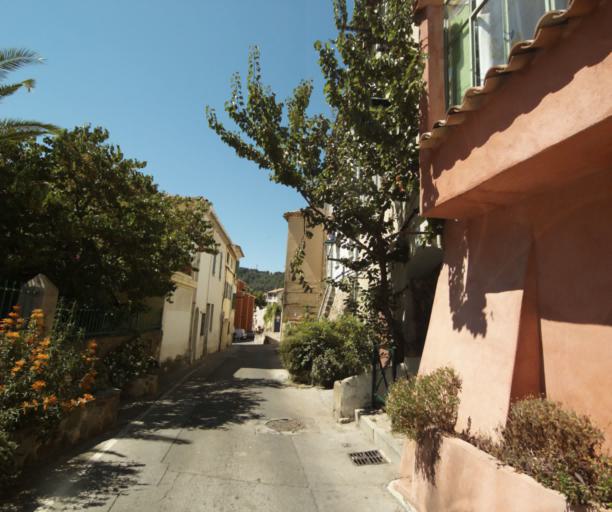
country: FR
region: Provence-Alpes-Cote d'Azur
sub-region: Departement du Var
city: La Garde
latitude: 43.1244
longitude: 6.0116
